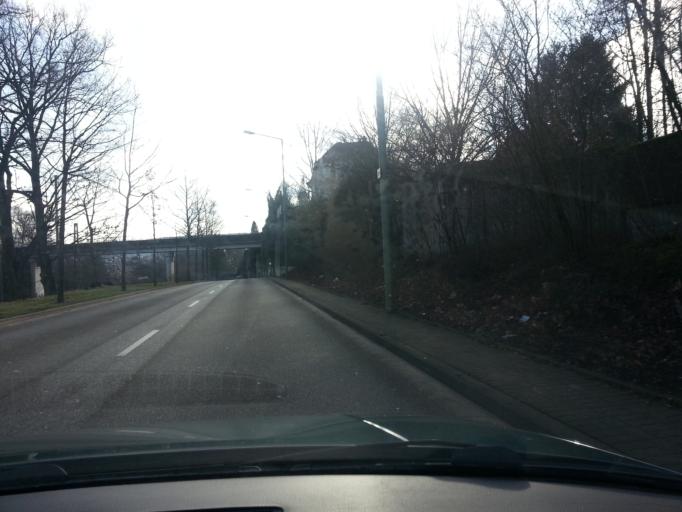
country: DE
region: Rheinland-Pfalz
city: Kaiserslautern
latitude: 49.4377
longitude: 7.7429
